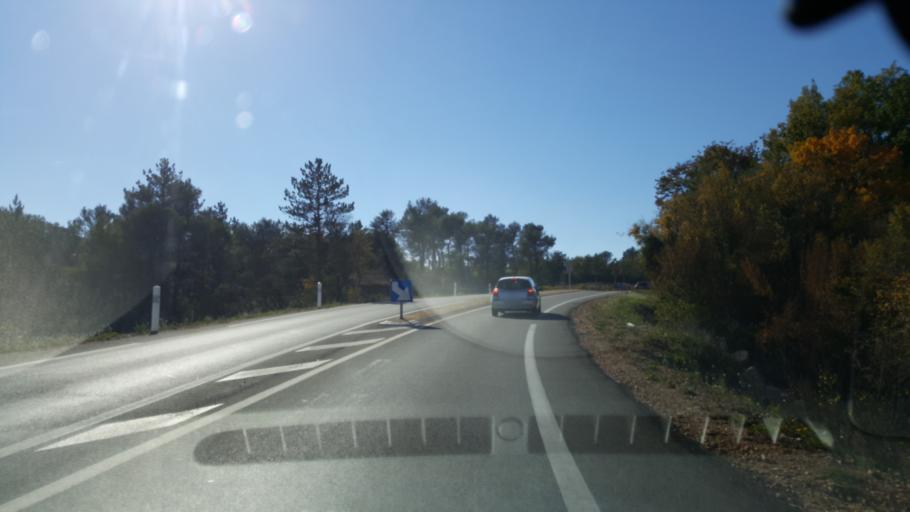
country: FR
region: Provence-Alpes-Cote d'Azur
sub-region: Departement du Var
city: Nans-les-Pins
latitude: 43.3936
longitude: 5.7990
